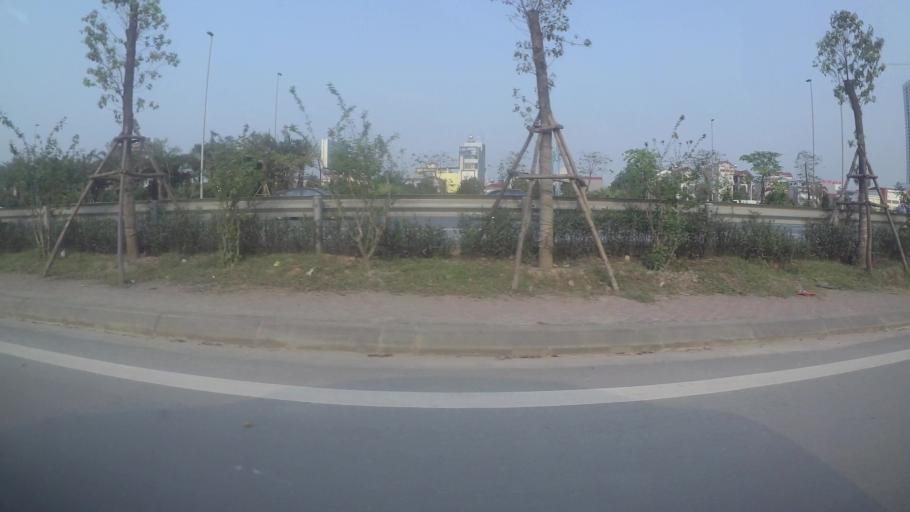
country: VN
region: Ha Noi
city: Dong Anh
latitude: 21.1157
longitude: 105.8268
